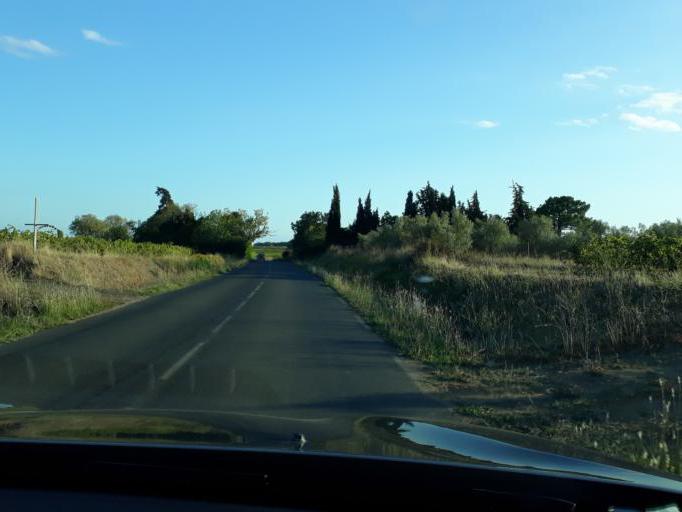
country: FR
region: Languedoc-Roussillon
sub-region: Departement de l'Herault
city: Pomerols
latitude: 43.3835
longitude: 3.4984
